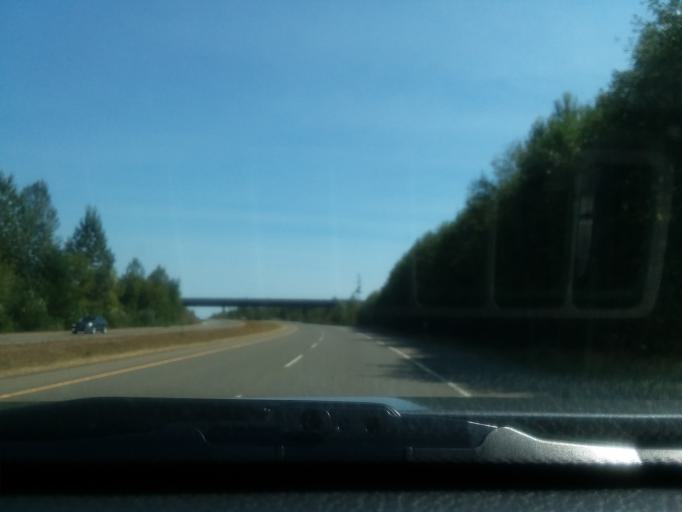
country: CA
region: British Columbia
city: Cumberland
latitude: 49.4888
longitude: -124.8324
